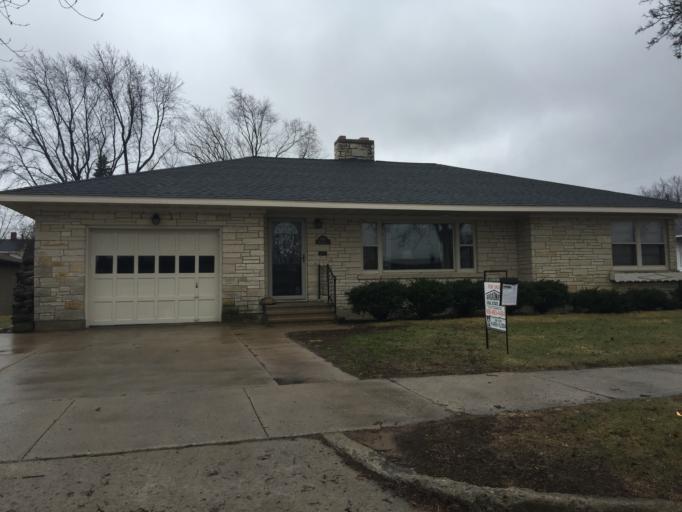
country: US
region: Michigan
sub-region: Menominee County
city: Menominee
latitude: 45.1152
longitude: -87.6259
